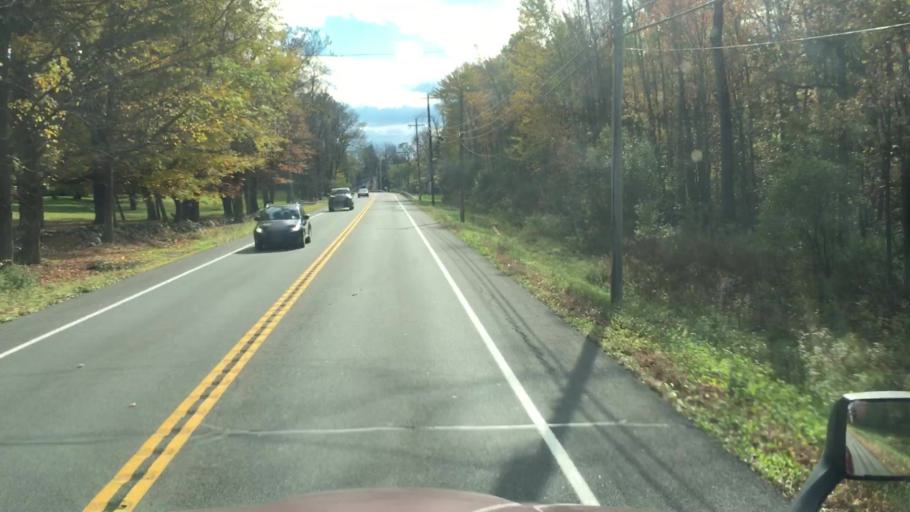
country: US
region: New York
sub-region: Saratoga County
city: Ballston Spa
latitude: 42.9607
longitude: -73.8644
